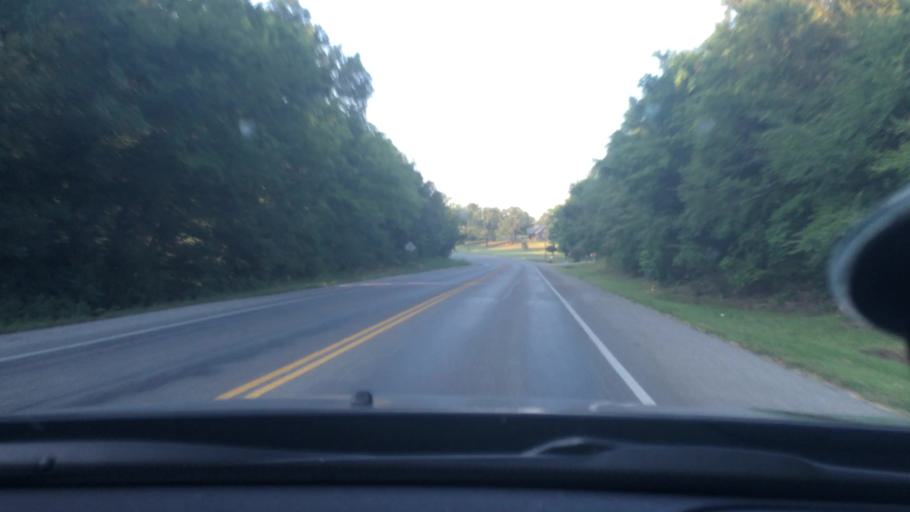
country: US
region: Oklahoma
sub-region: Pontotoc County
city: Byng
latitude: 34.8366
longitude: -96.6788
